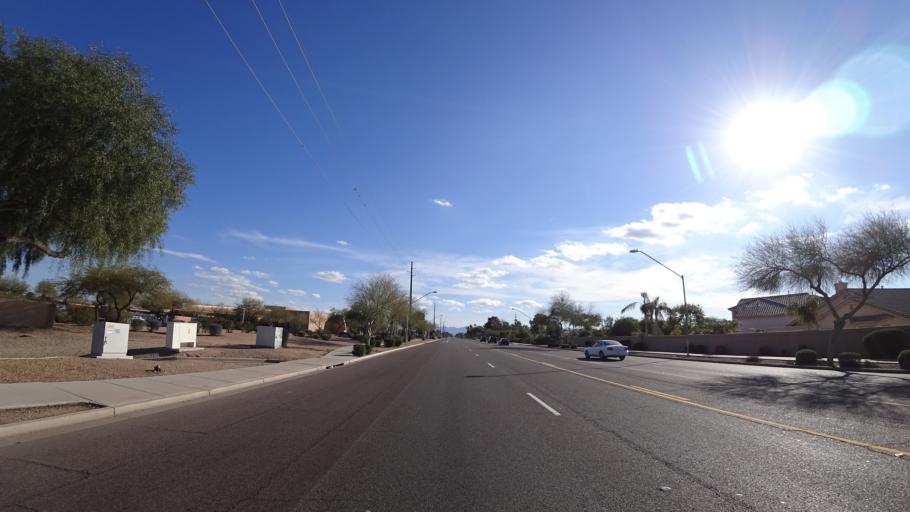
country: US
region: Arizona
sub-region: Maricopa County
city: Peoria
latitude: 33.5288
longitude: -112.2376
